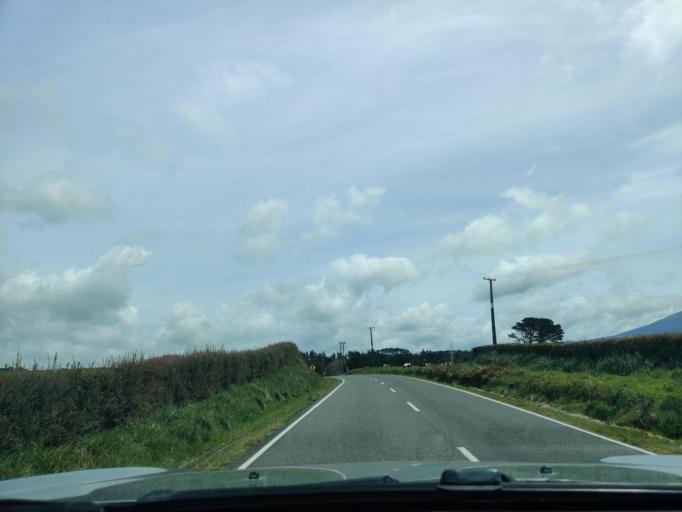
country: NZ
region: Taranaki
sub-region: South Taranaki District
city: Eltham
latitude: -39.3714
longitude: 174.1962
